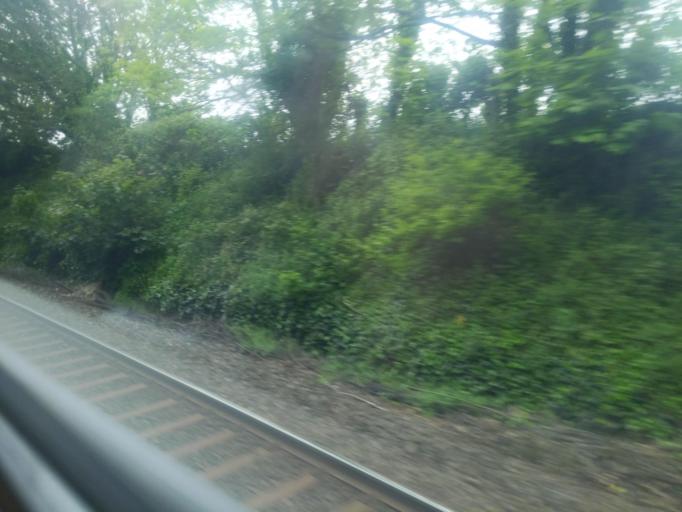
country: GB
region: England
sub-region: Cornwall
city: Hayle
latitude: 50.1818
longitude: -5.4276
